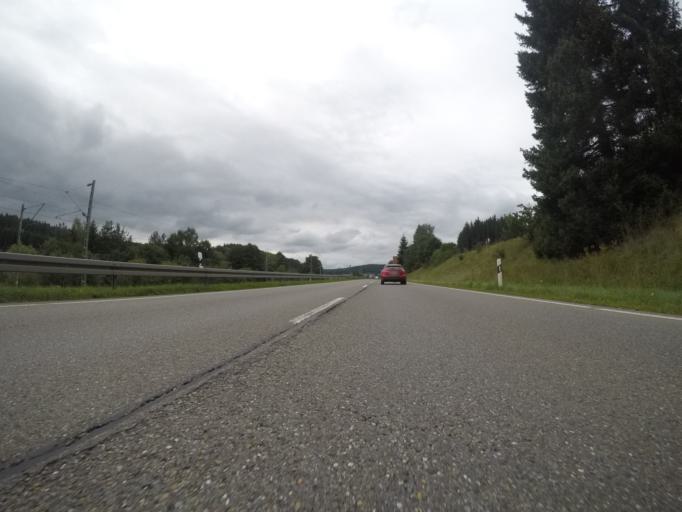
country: DE
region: Baden-Wuerttemberg
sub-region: Freiburg Region
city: Konigsfeld im Schwarzwald
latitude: 48.1253
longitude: 8.3857
